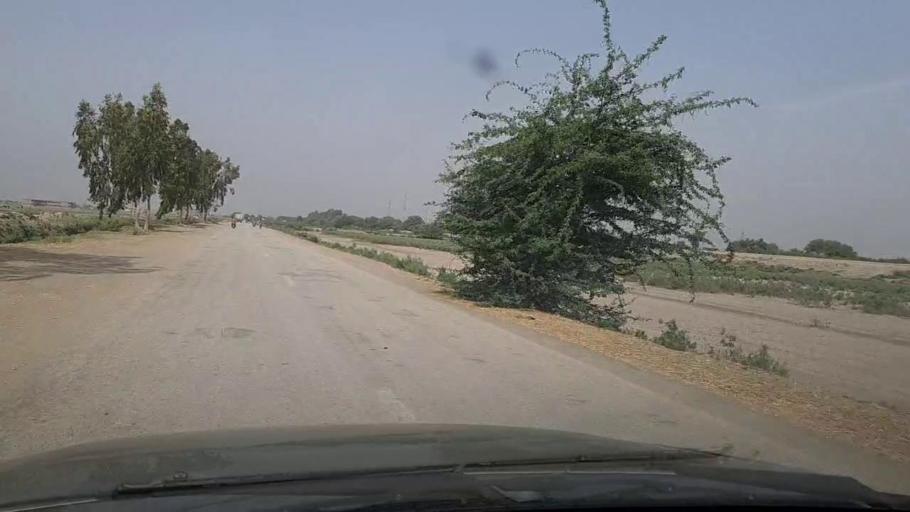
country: PK
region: Sindh
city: Thul
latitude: 28.3226
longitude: 68.7478
